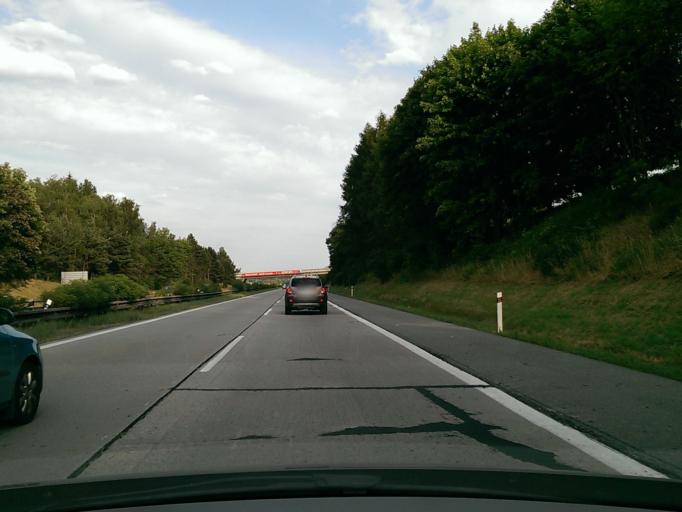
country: CZ
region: Vysocina
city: Velky Beranov
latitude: 49.4362
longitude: 15.6438
